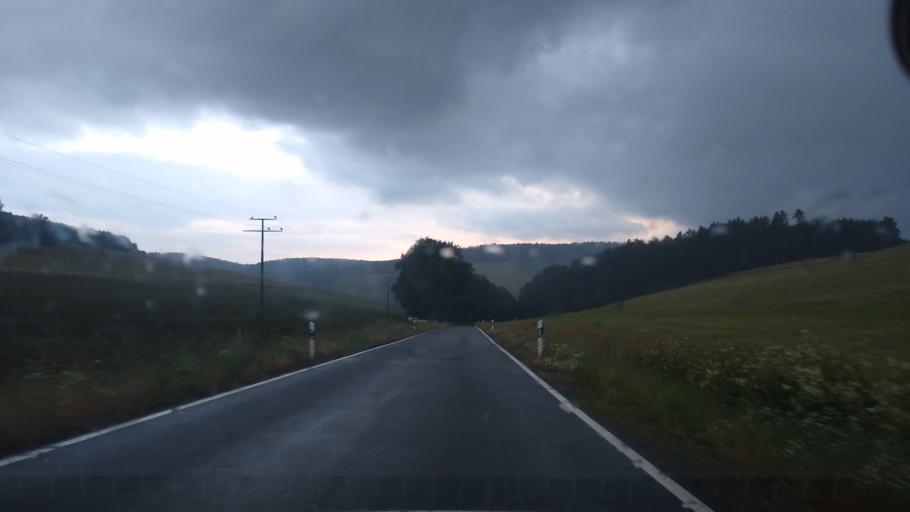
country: DE
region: Hesse
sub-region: Regierungsbezirk Darmstadt
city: Erbach
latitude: 49.6510
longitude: 8.9431
